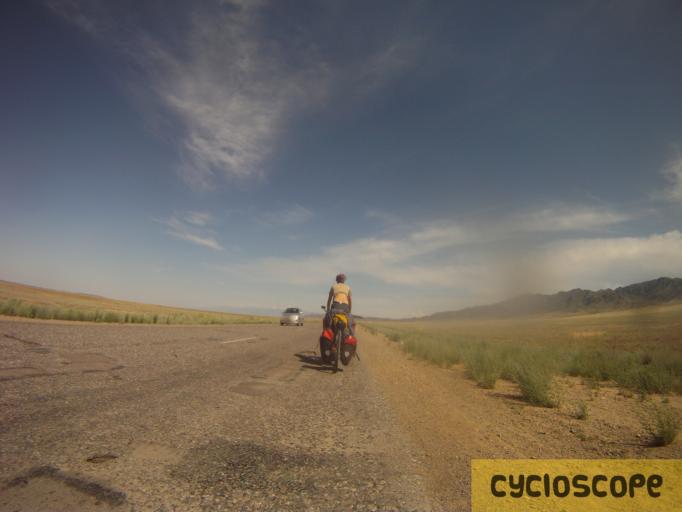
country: KZ
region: Almaty Oblysy
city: Kegen
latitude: 43.3837
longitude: 78.8472
